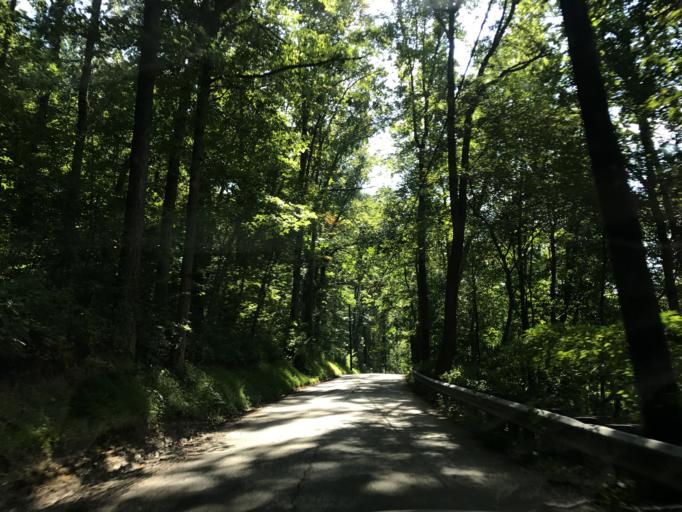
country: US
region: Maryland
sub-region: Harford County
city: Jarrettsville
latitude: 39.6268
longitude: -76.5954
